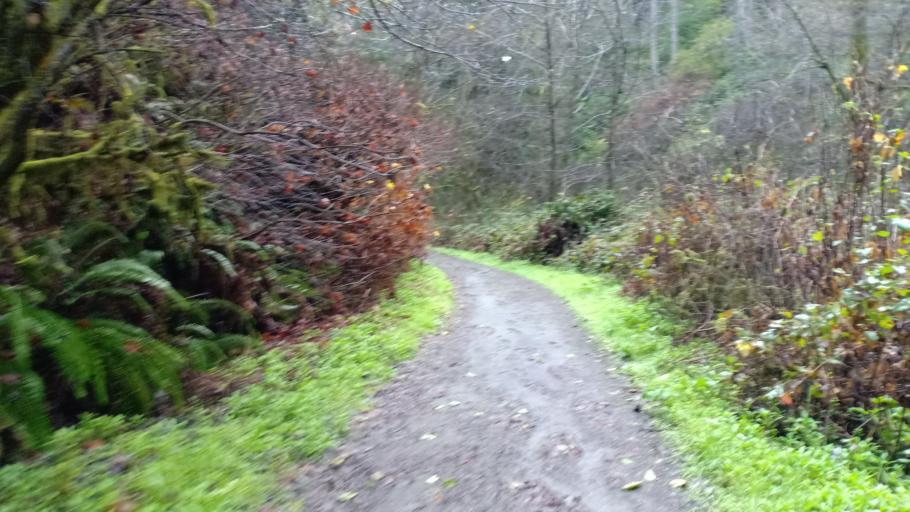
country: US
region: California
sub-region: Mendocino County
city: Fort Bragg
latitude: 39.2766
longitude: -123.7804
